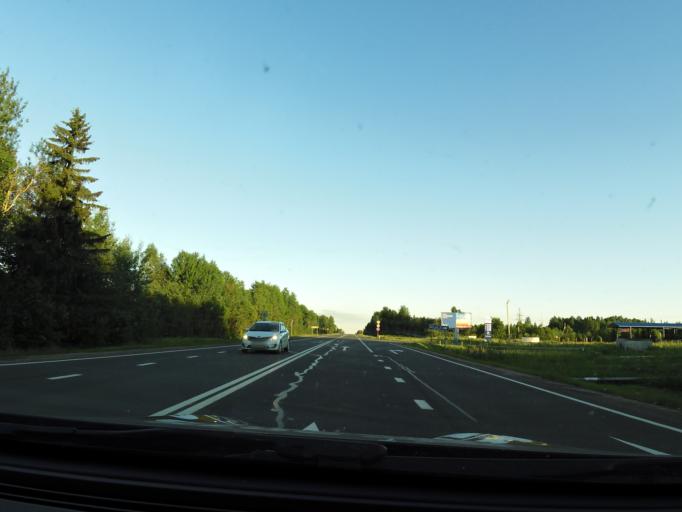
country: RU
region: Vologda
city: Gryazovets
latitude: 58.7852
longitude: 40.2705
